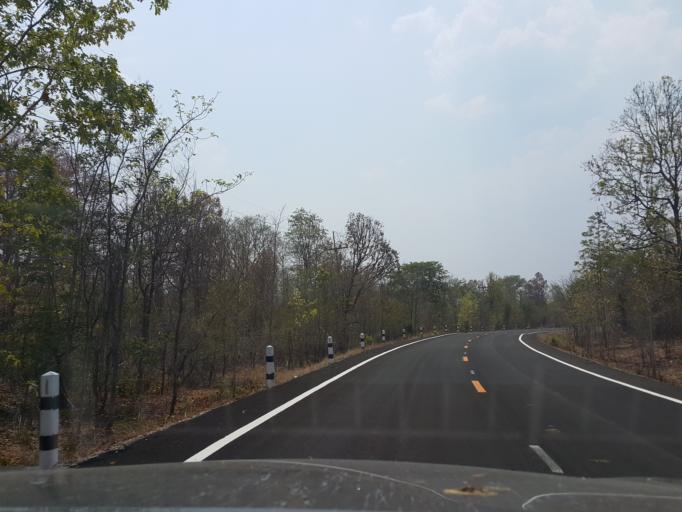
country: TH
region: Lampang
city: Mae Phrik
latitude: 17.4796
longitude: 99.1117
